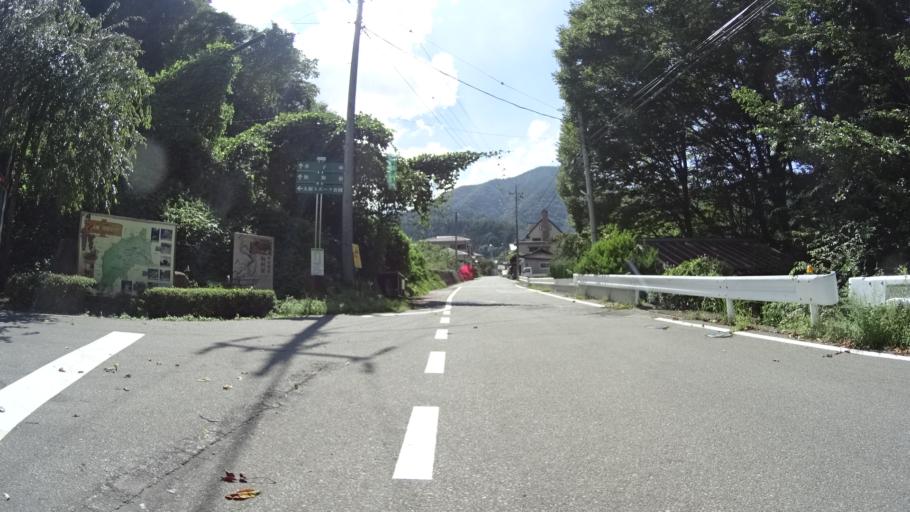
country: JP
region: Yamanashi
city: Enzan
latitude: 35.6379
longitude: 138.7725
